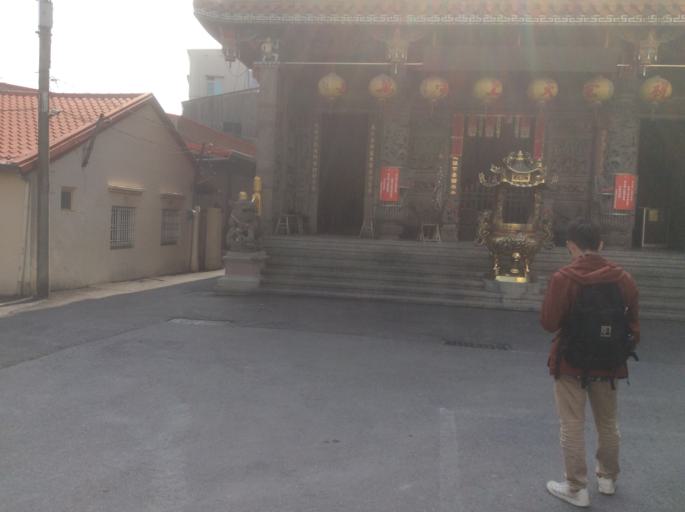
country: TW
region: Taiwan
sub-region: Tainan
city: Tainan
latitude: 22.9910
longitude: 120.2342
